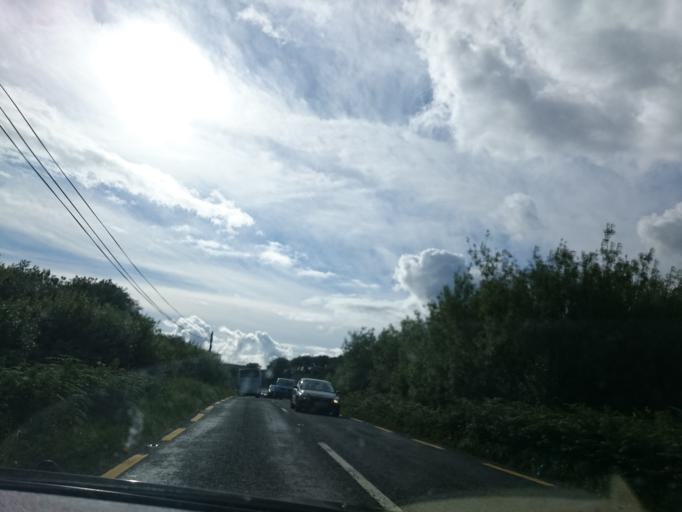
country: IE
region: Connaught
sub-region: Maigh Eo
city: Westport
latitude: 53.9014
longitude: -9.6136
